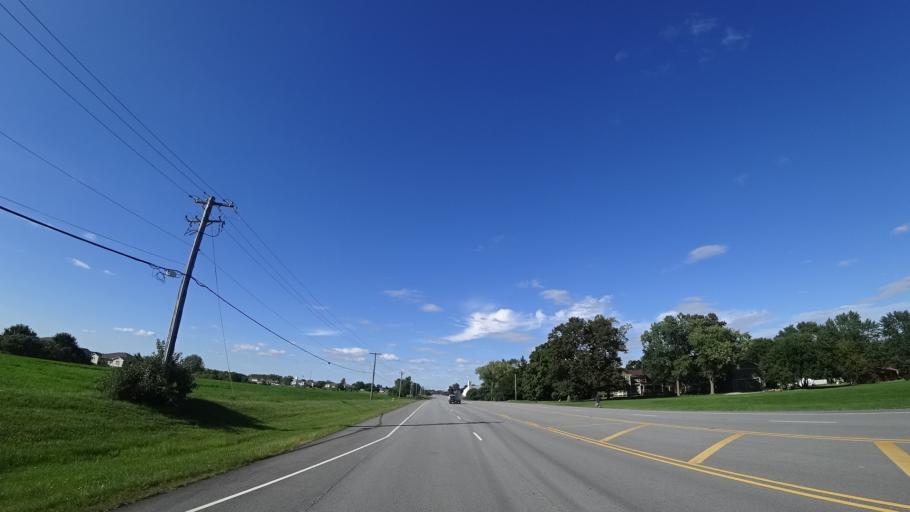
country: US
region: Illinois
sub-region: Cook County
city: Country Club Hills
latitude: 41.5621
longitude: -87.7333
